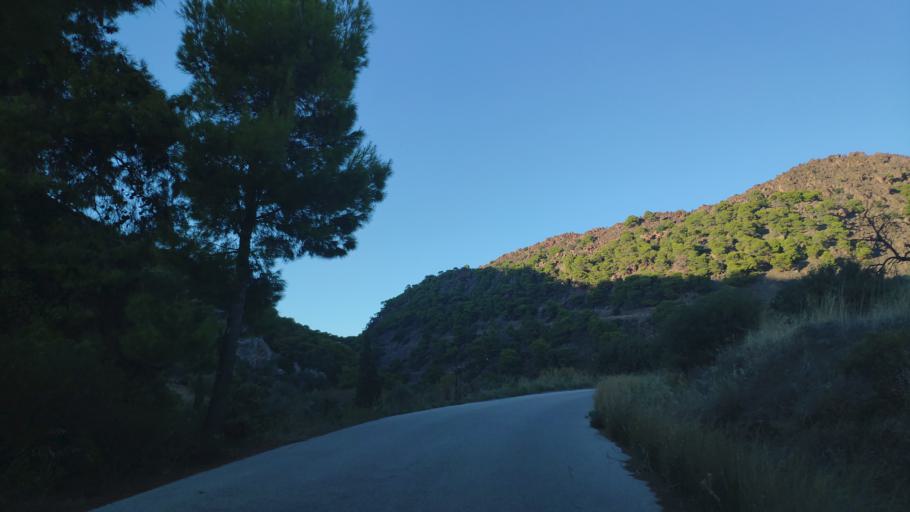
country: GR
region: Attica
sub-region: Nomos Piraios
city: Megalochori
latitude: 37.6118
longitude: 23.3277
